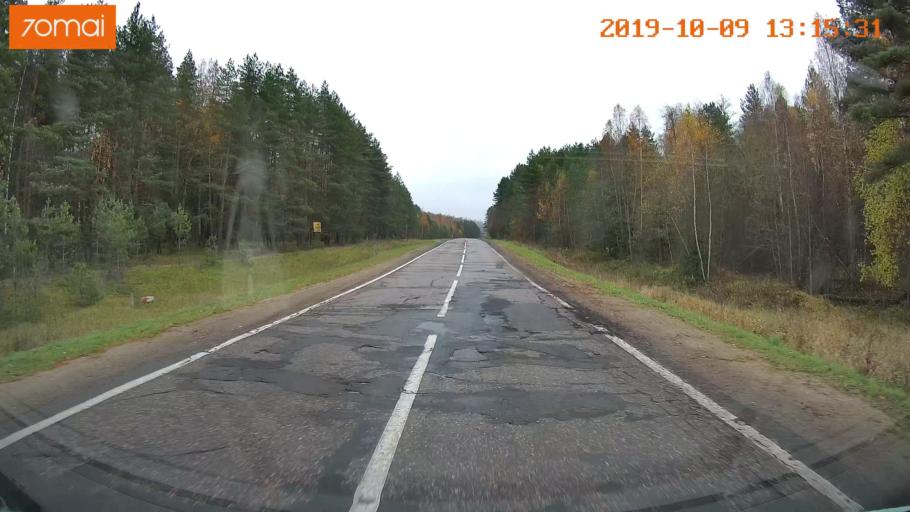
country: RU
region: Jaroslavl
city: Lyubim
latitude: 58.3671
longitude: 40.7532
